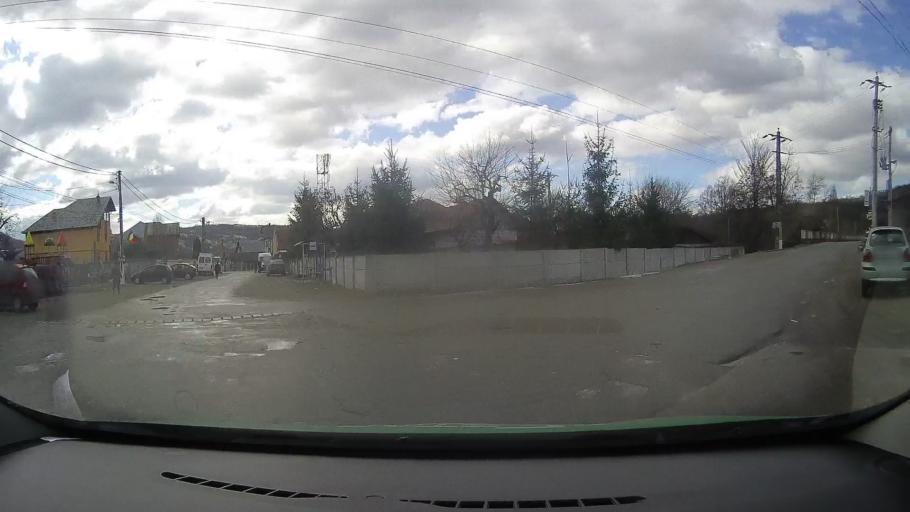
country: RO
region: Dambovita
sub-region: Comuna Buciumeni
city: Buciumeni
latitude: 45.1522
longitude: 25.4512
